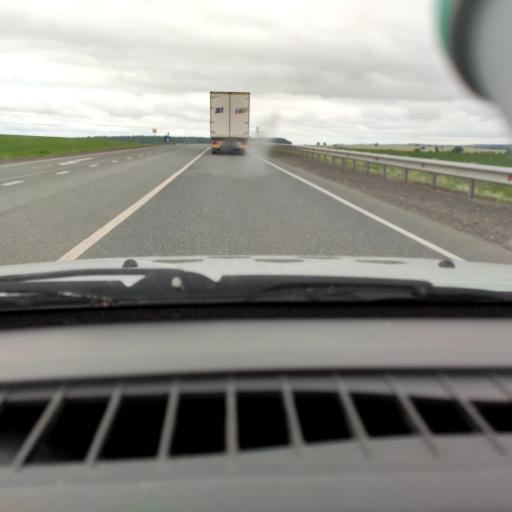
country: RU
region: Udmurtiya
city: Alnashi
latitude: 56.1145
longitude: 52.4611
